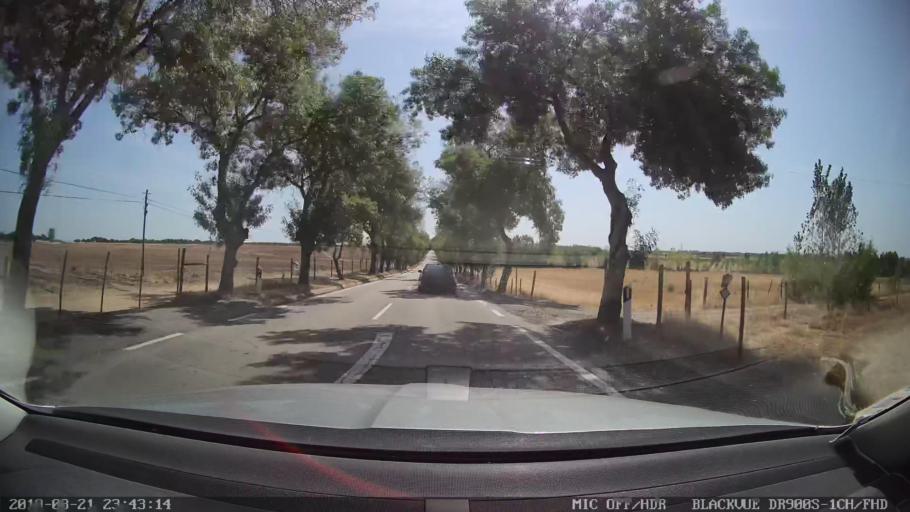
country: PT
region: Castelo Branco
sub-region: Idanha-A-Nova
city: Idanha-a-Nova
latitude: 39.8510
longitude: -7.2992
